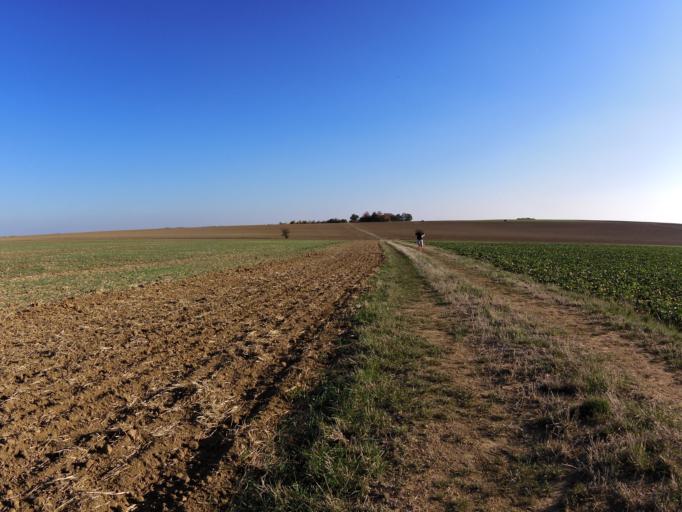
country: DE
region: Bavaria
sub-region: Regierungsbezirk Unterfranken
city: Eibelstadt
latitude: 49.7048
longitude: 9.9851
